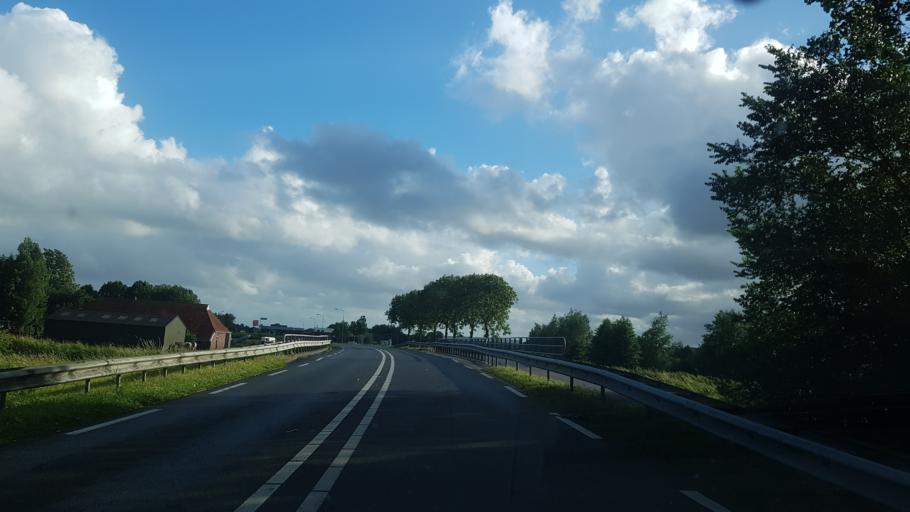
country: NL
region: Groningen
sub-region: Gemeente Bedum
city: Bedum
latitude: 53.2841
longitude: 6.7118
